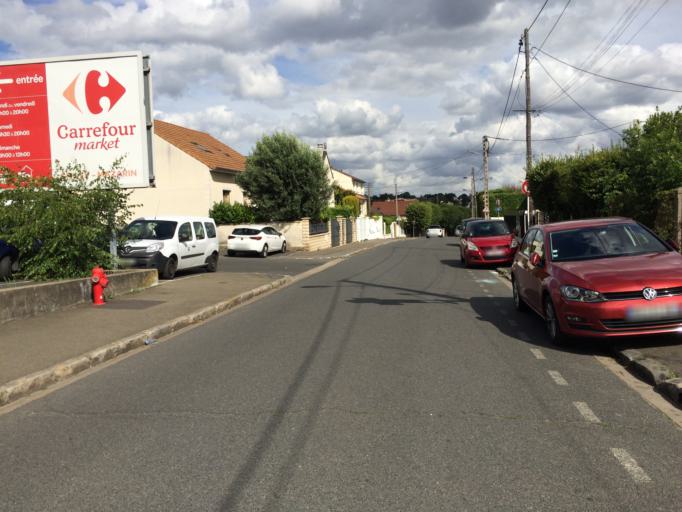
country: FR
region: Ile-de-France
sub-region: Departement de l'Essonne
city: Longjumeau
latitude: 48.6999
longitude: 2.3190
